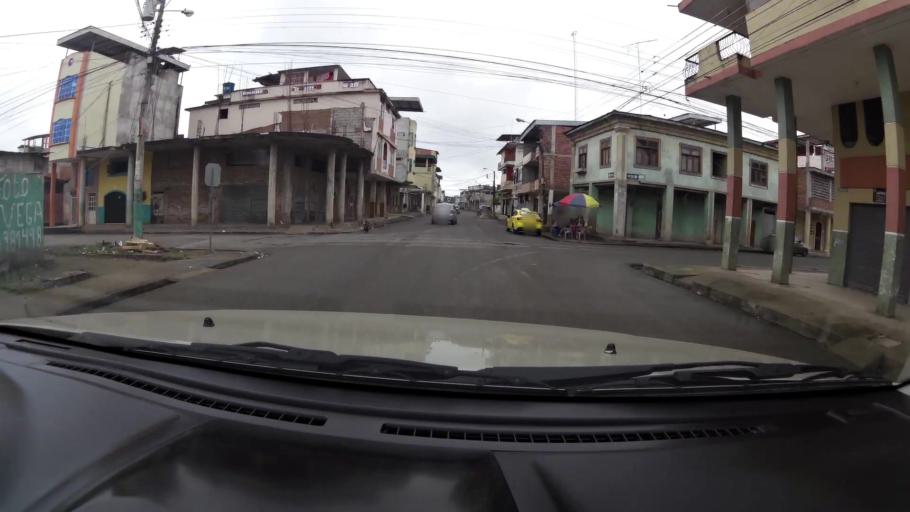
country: EC
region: El Oro
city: Pasaje
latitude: -3.3249
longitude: -79.8061
